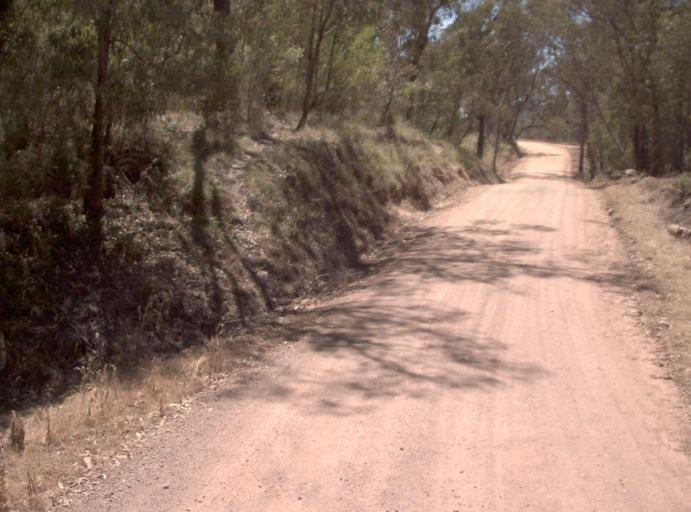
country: AU
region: New South Wales
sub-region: Snowy River
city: Jindabyne
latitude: -36.9705
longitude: 148.3033
